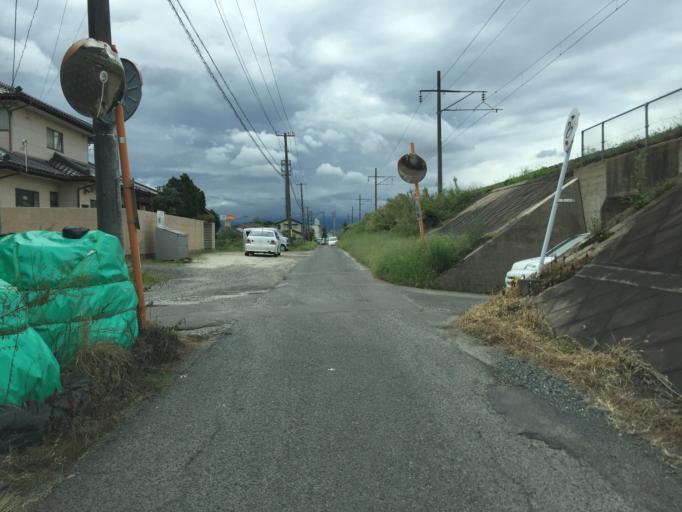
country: JP
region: Fukushima
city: Fukushima-shi
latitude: 37.8002
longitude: 140.4928
